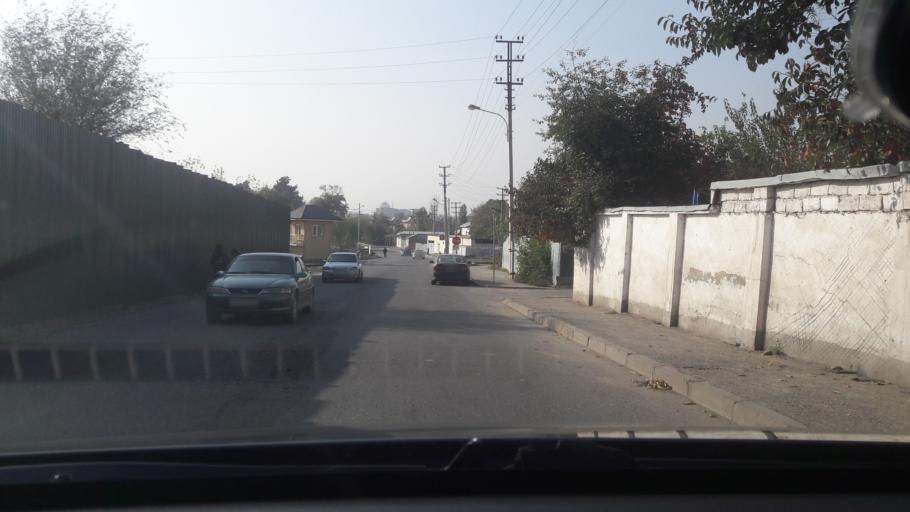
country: TJ
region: Dushanbe
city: Dushanbe
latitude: 38.5629
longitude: 68.7819
